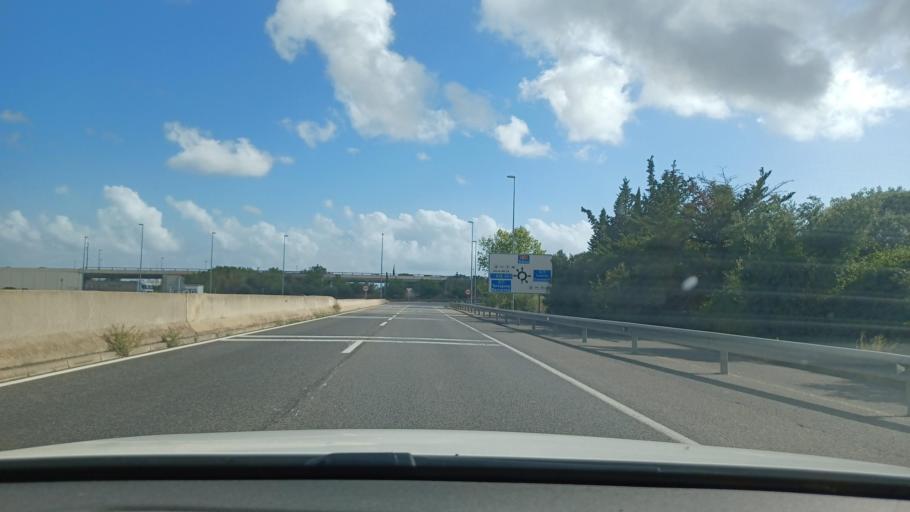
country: ES
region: Catalonia
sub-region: Provincia de Tarragona
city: Vila-seca
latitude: 41.1050
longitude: 1.1270
